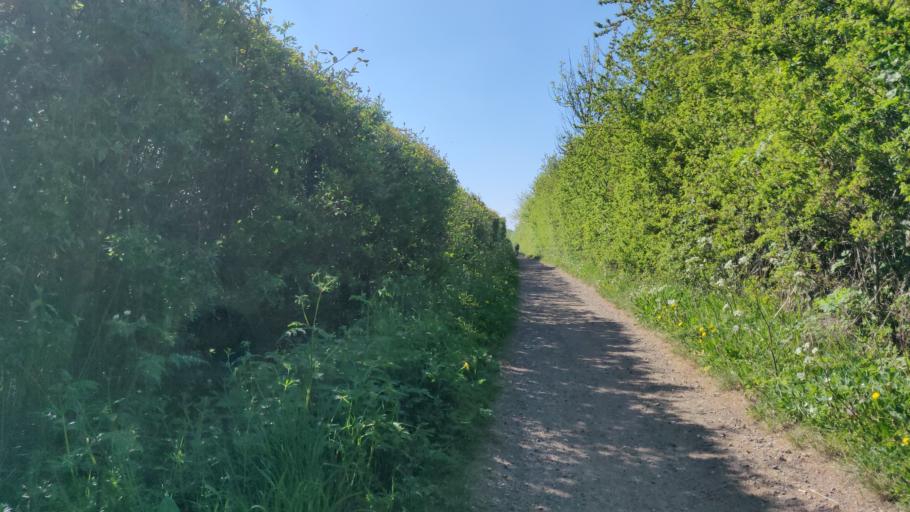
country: GB
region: England
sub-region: West Sussex
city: Southwater
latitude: 51.0620
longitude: -0.3921
